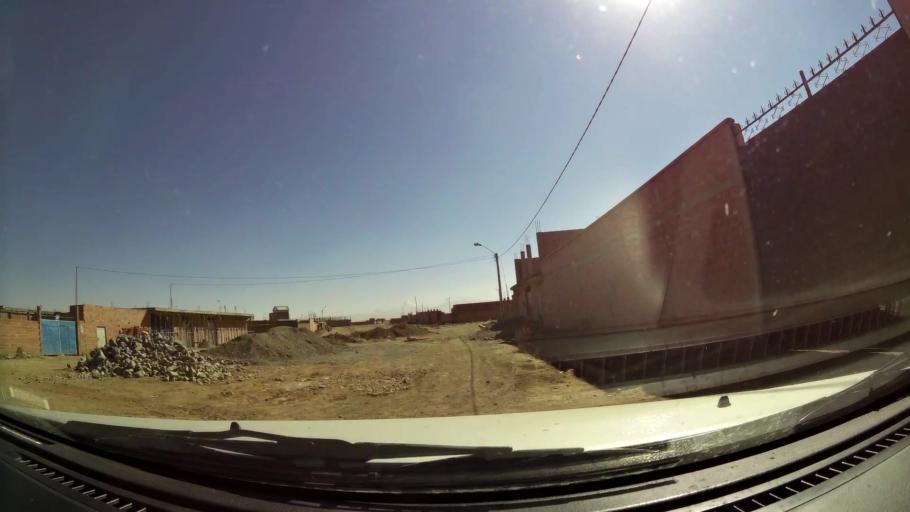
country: BO
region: La Paz
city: La Paz
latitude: -16.6172
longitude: -68.1938
